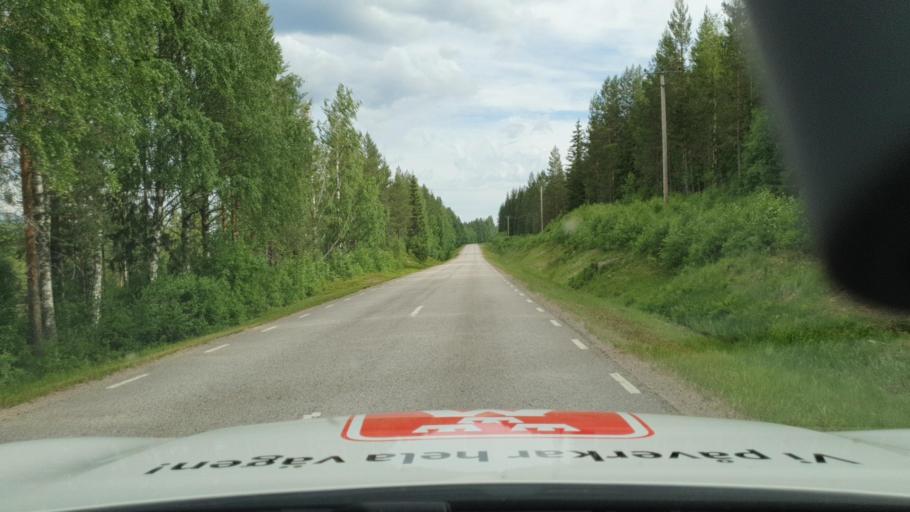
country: NO
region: Hedmark
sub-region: Trysil
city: Innbygda
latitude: 61.0129
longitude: 12.4775
